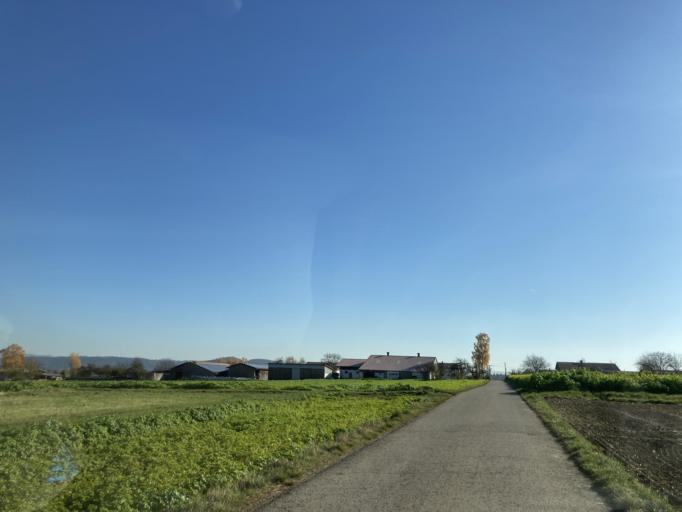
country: DE
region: Baden-Wuerttemberg
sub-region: Tuebingen Region
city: Rottenburg
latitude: 48.4770
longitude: 8.8883
